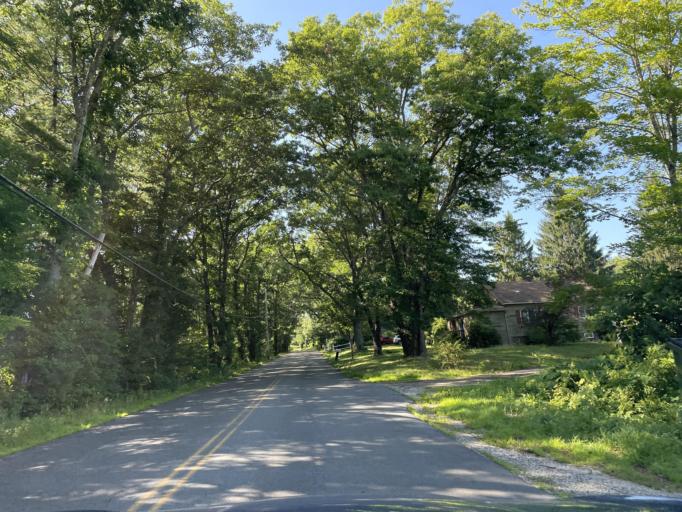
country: US
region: Massachusetts
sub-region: Worcester County
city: Charlton
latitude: 42.1640
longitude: -72.0244
